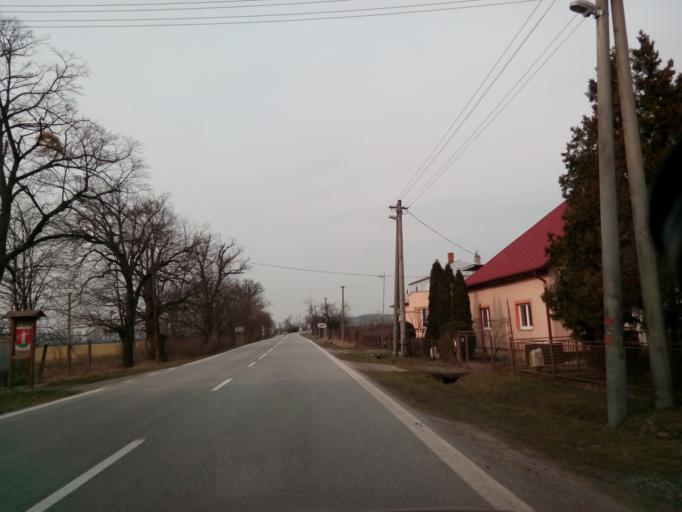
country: HU
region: Borsod-Abauj-Zemplen
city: Satoraljaujhely
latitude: 48.4652
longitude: 21.6395
